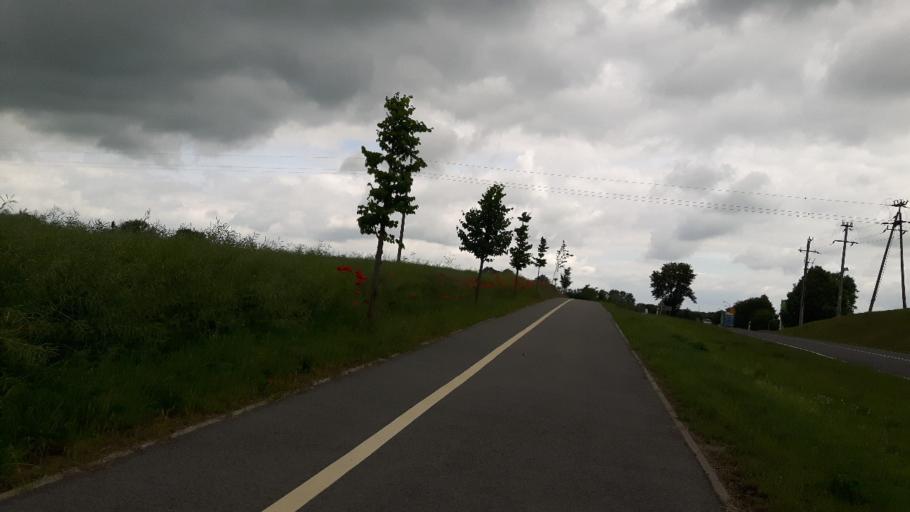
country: PL
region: West Pomeranian Voivodeship
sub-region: Powiat policki
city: Kolbaskowo
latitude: 53.3322
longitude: 14.4305
